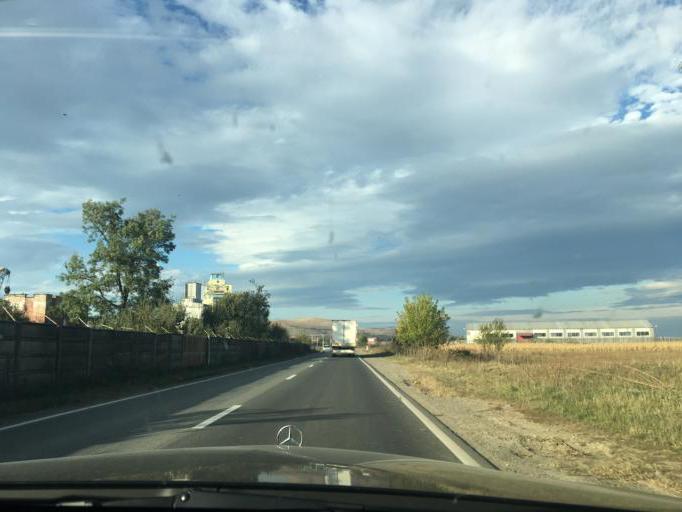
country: RO
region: Alba
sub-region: Municipiul Alba Iulia
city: Barabant
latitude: 46.0838
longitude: 23.5971
